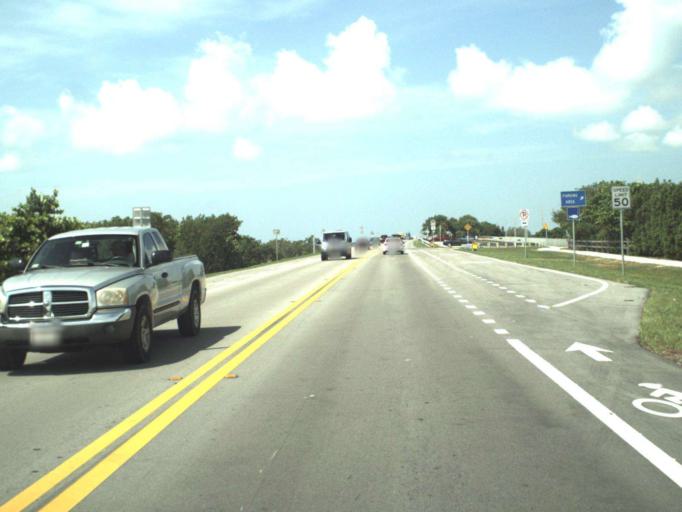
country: US
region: Florida
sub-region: Monroe County
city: Islamorada
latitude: 24.8465
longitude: -80.7452
